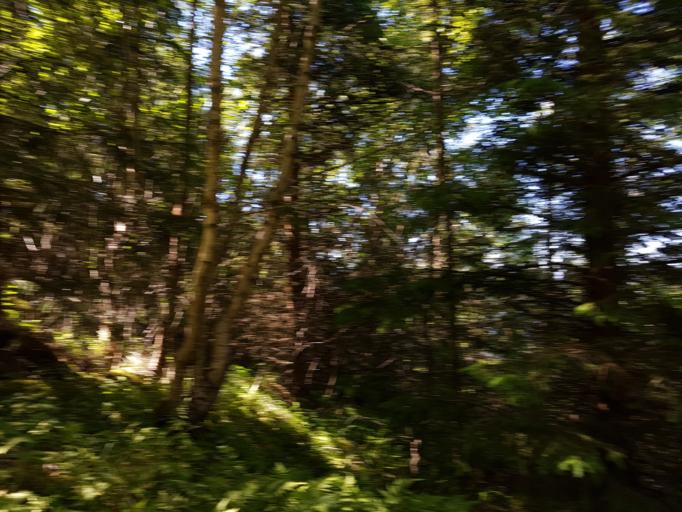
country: NO
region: Sor-Trondelag
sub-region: Melhus
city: Melhus
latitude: 63.4403
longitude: 10.2091
